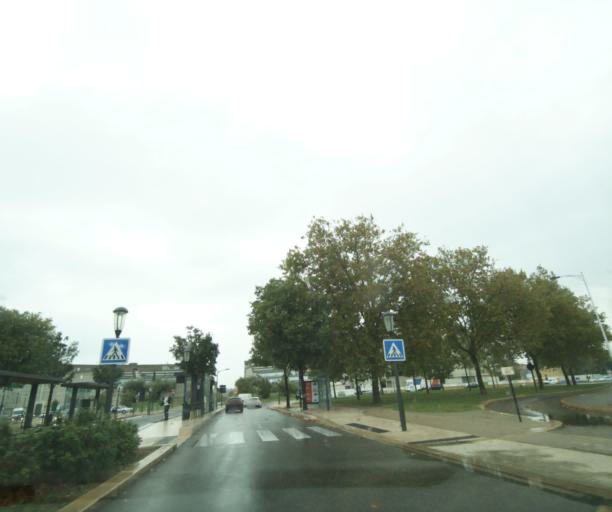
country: FR
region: Languedoc-Roussillon
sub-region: Departement du Gard
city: Nimes
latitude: 43.8193
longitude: 4.3590
